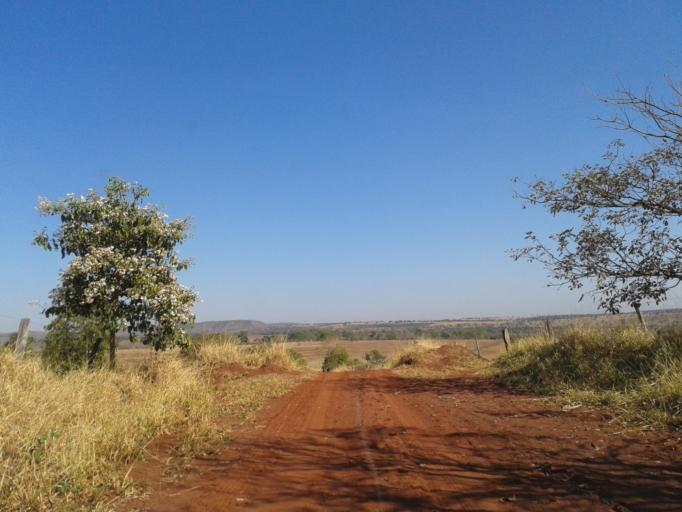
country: BR
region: Minas Gerais
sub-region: Santa Vitoria
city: Santa Vitoria
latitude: -19.0467
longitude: -49.9444
